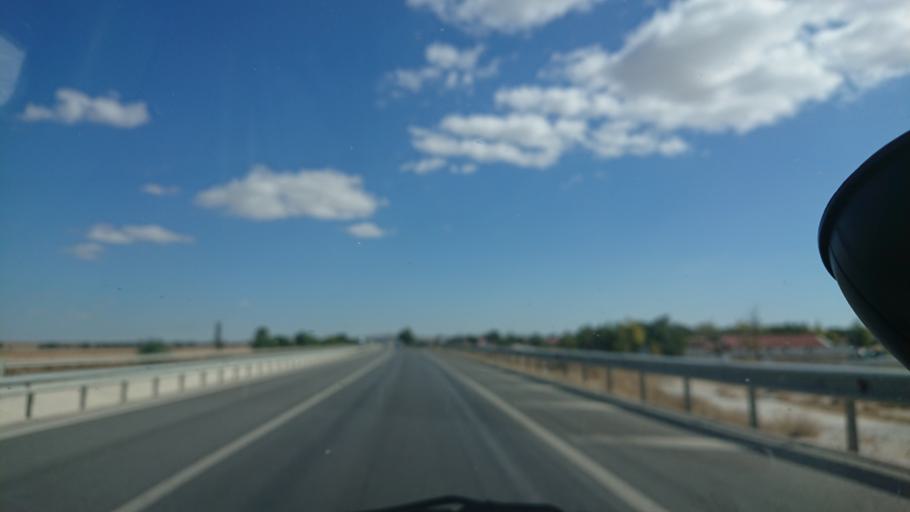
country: TR
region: Eskisehir
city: Mahmudiye
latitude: 39.5434
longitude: 30.9352
